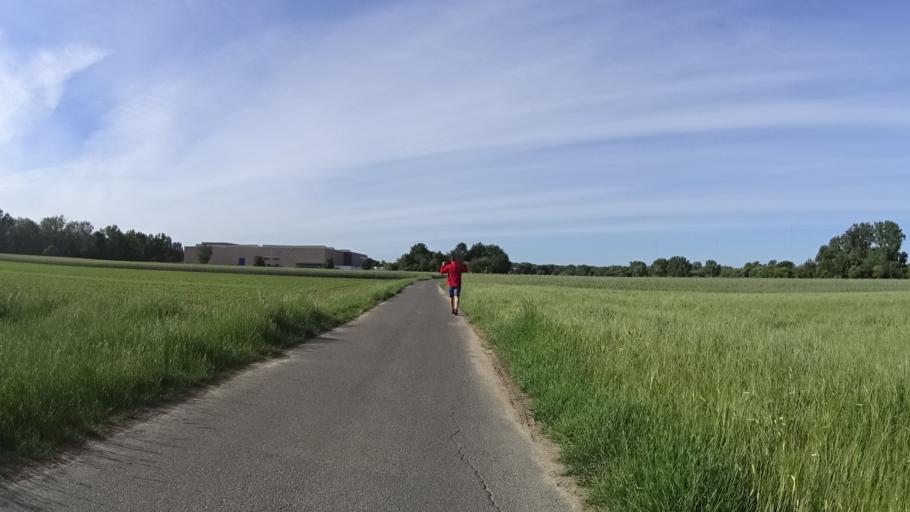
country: DE
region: Bavaria
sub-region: Regierungsbezirk Unterfranken
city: Kleinostheim
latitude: 50.0314
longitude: 9.0350
